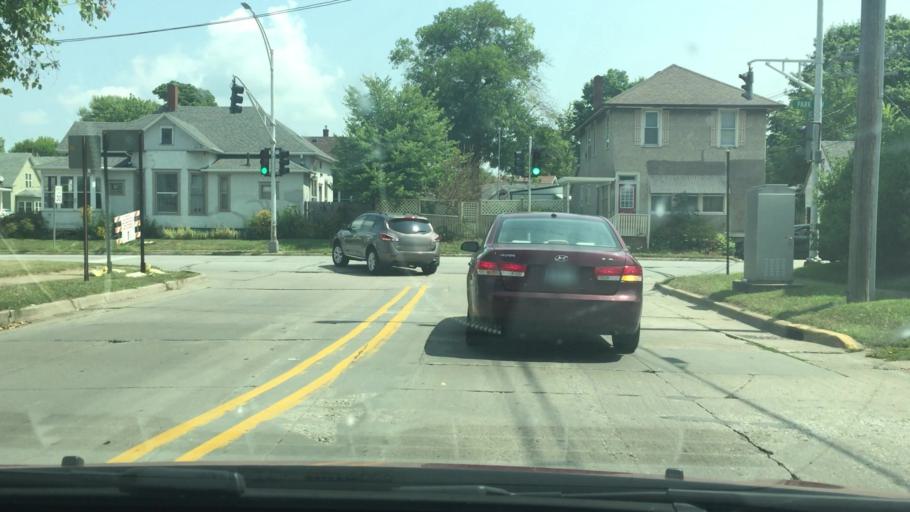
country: US
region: Iowa
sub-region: Muscatine County
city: Muscatine
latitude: 41.4308
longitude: -91.0315
